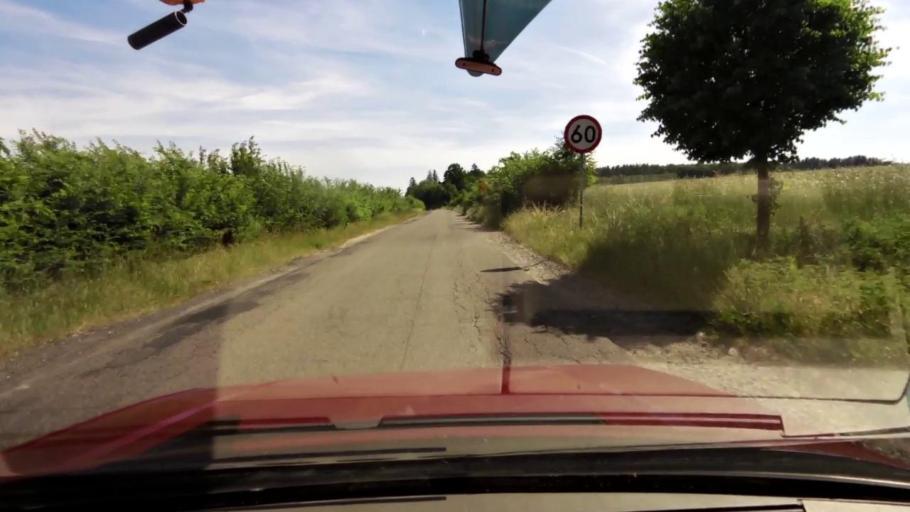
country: PL
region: Pomeranian Voivodeship
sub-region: Powiat slupski
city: Kobylnica
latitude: 54.3764
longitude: 16.9657
